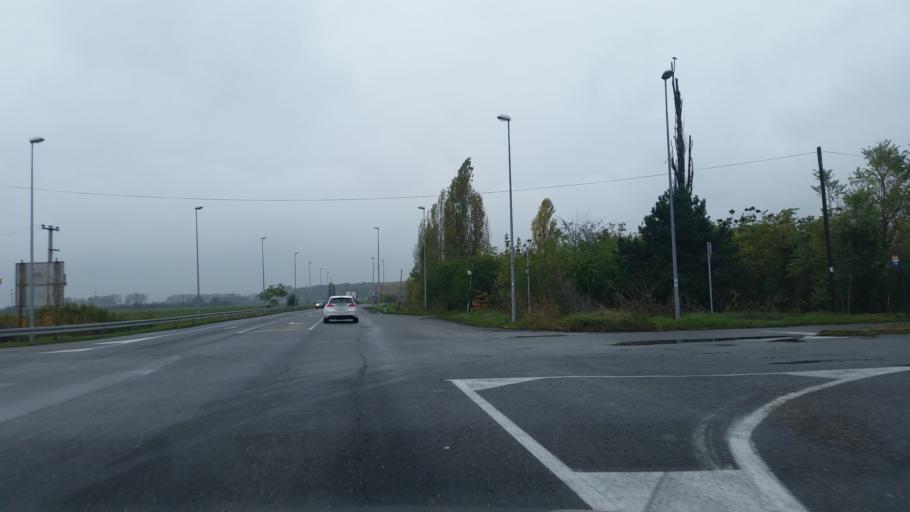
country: RS
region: Central Serbia
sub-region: Belgrade
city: Zemun
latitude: 44.9162
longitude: 20.4416
